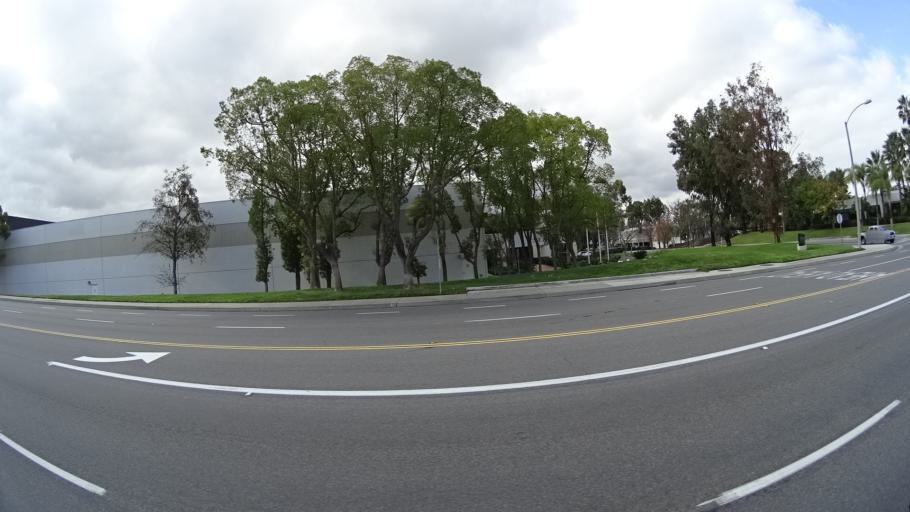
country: US
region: California
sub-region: Orange County
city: Lake Forest
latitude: 33.6509
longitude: -117.7083
